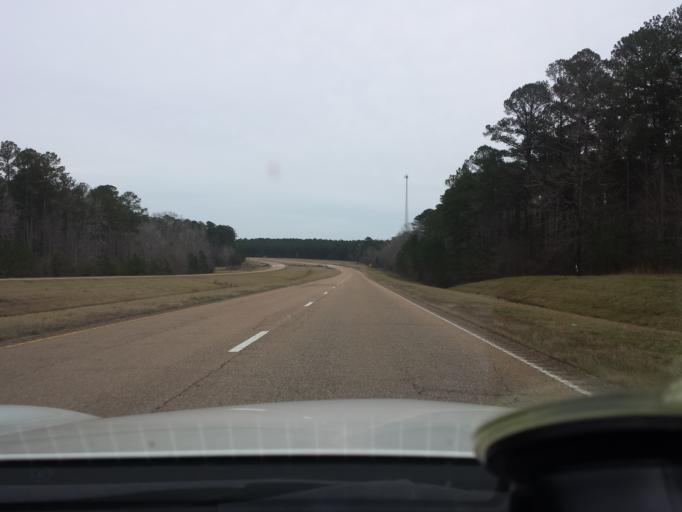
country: US
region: Mississippi
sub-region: Oktibbeha County
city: Starkville
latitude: 33.3447
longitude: -88.8847
